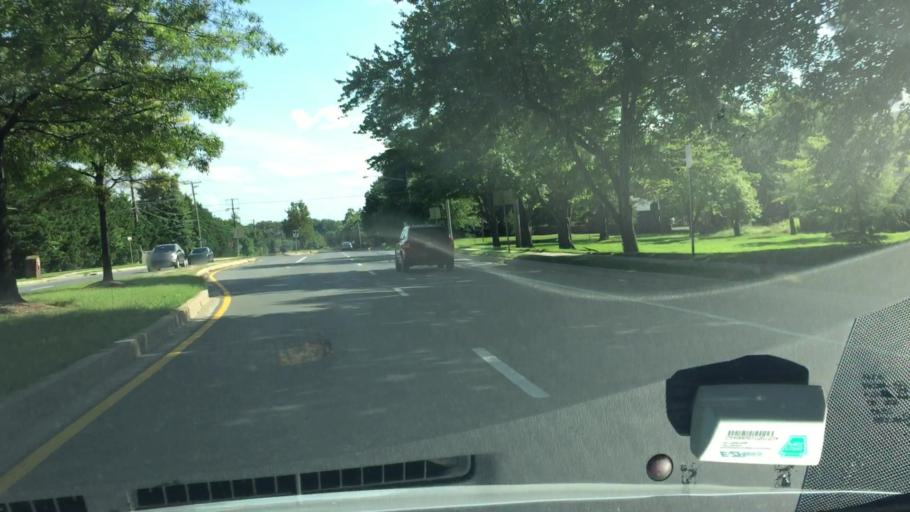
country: US
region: Maryland
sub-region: Montgomery County
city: Layhill
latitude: 39.0863
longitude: -77.0455
